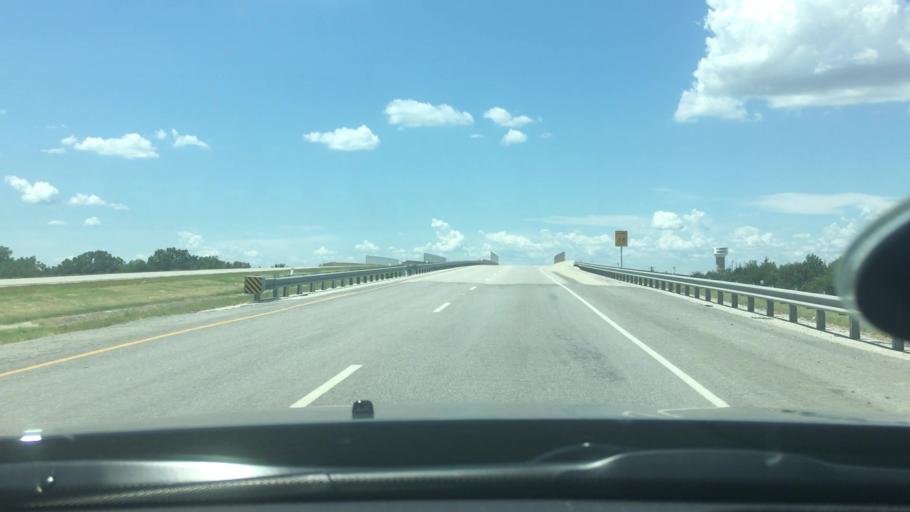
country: US
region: Oklahoma
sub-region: Bryan County
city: Durant
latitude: 33.9656
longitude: -96.3921
